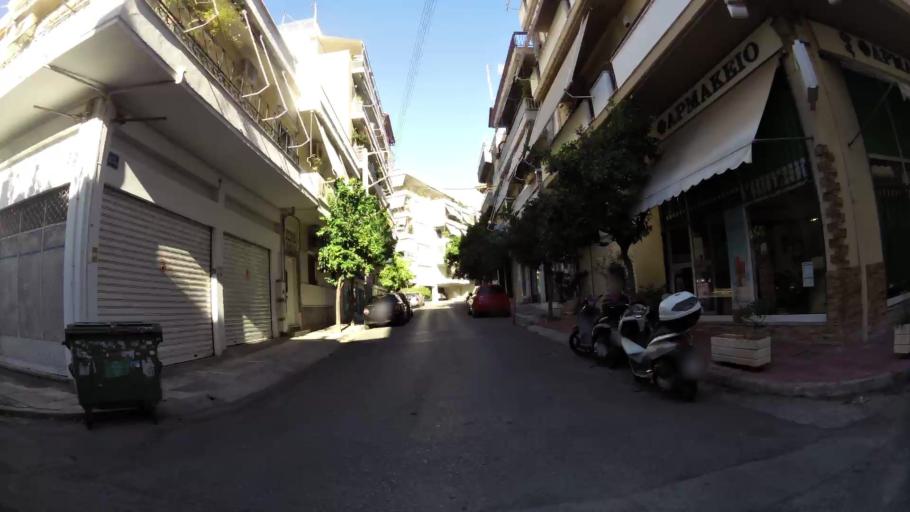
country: GR
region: Attica
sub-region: Nomos Piraios
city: Nikaia
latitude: 37.9707
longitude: 23.6562
